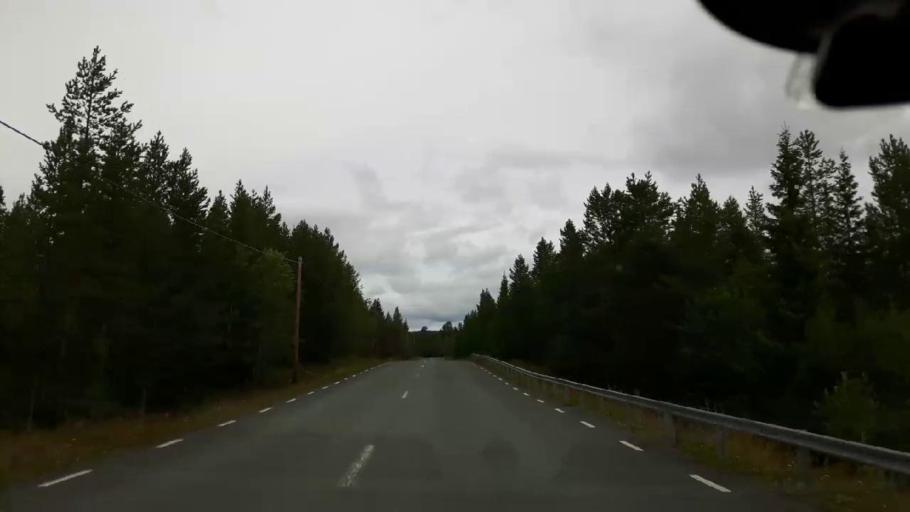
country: SE
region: Jaemtland
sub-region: Krokoms Kommun
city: Valla
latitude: 63.6759
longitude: 13.8696
